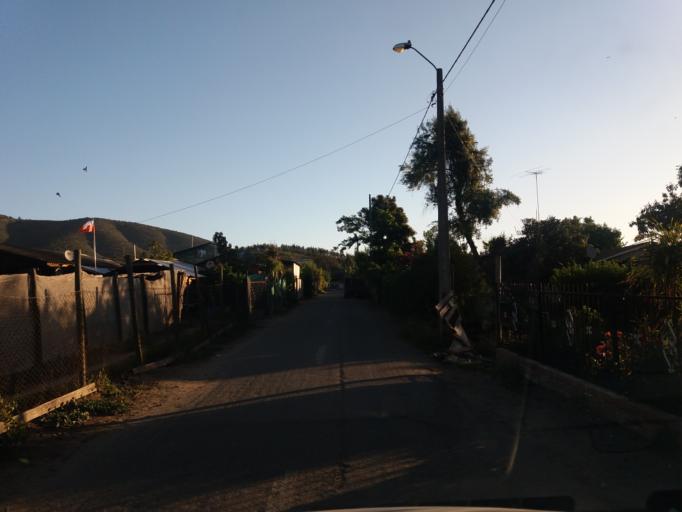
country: CL
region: Valparaiso
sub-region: Provincia de Quillota
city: Quillota
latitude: -32.9453
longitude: -71.2739
